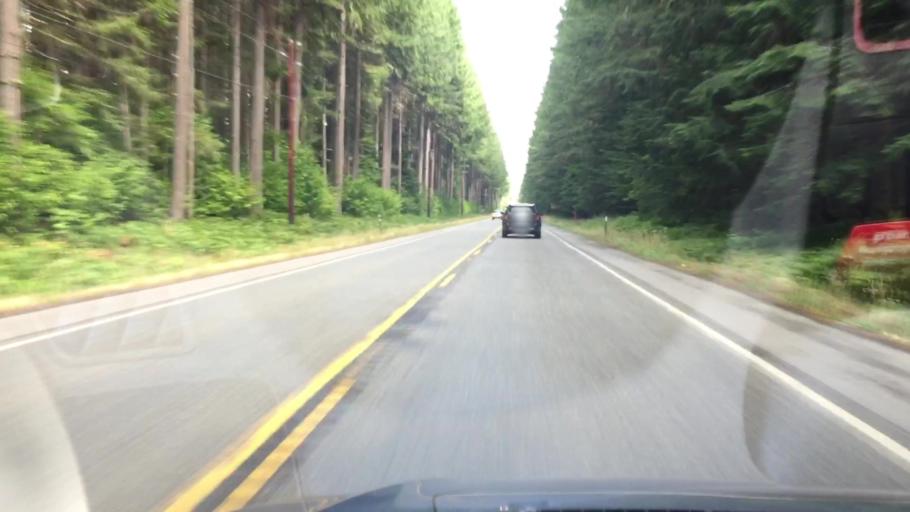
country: US
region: Washington
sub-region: Pierce County
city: Eatonville
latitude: 46.7560
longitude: -122.0919
